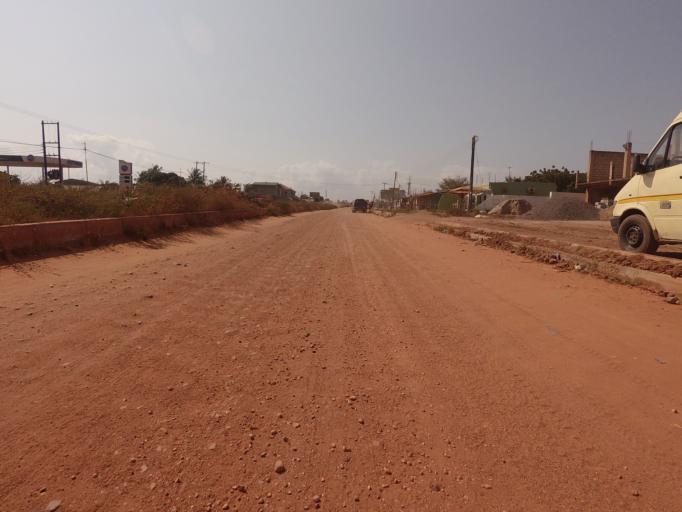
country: GH
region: Greater Accra
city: Teshi Old Town
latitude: 5.6110
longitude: -0.1235
